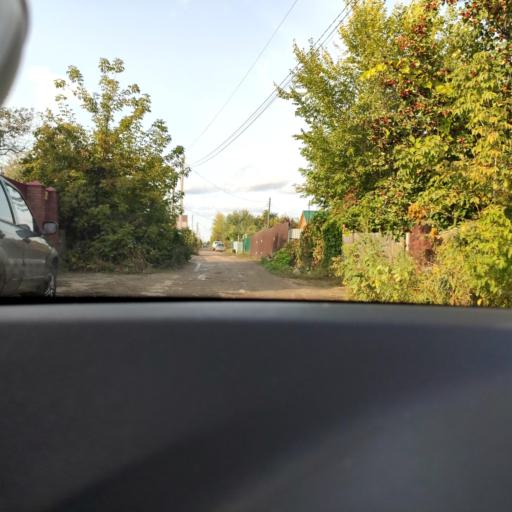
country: RU
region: Samara
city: Petra-Dubrava
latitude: 53.2840
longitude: 50.2950
